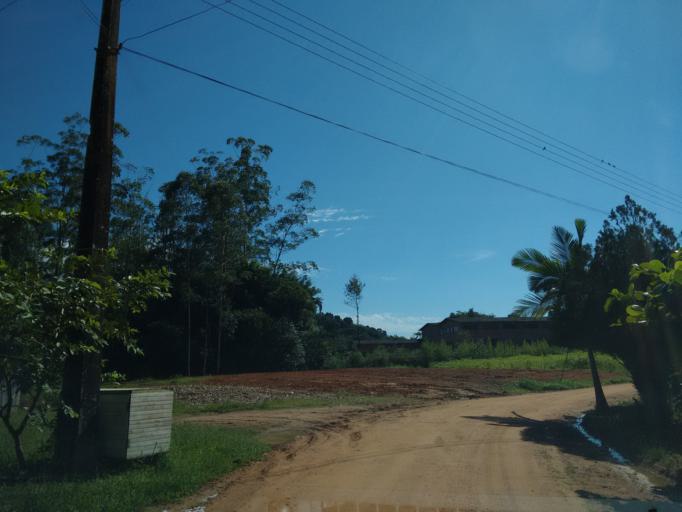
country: BR
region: Santa Catarina
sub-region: Pomerode
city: Pomerode
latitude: -26.7708
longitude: -49.1795
